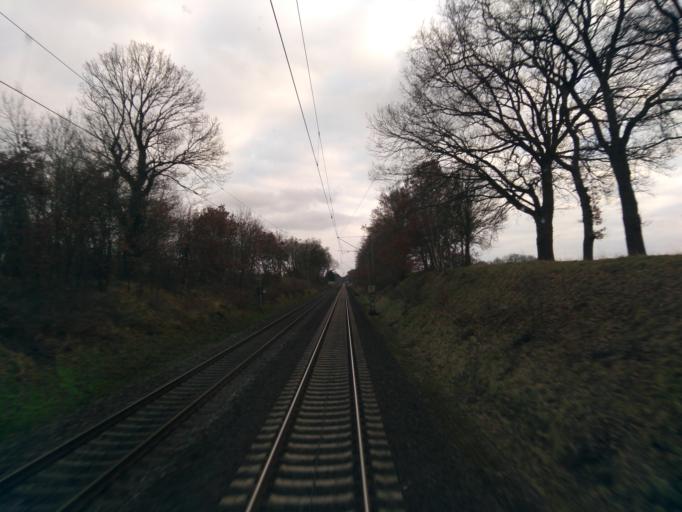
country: DE
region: Lower Saxony
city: Jelmstorf
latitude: 53.1052
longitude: 10.5442
